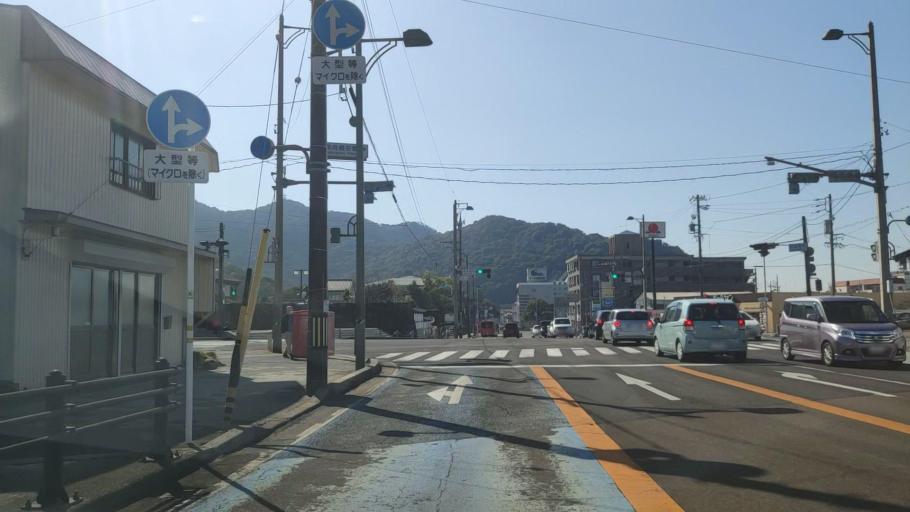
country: JP
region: Gifu
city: Gifu-shi
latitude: 35.4362
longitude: 136.7732
